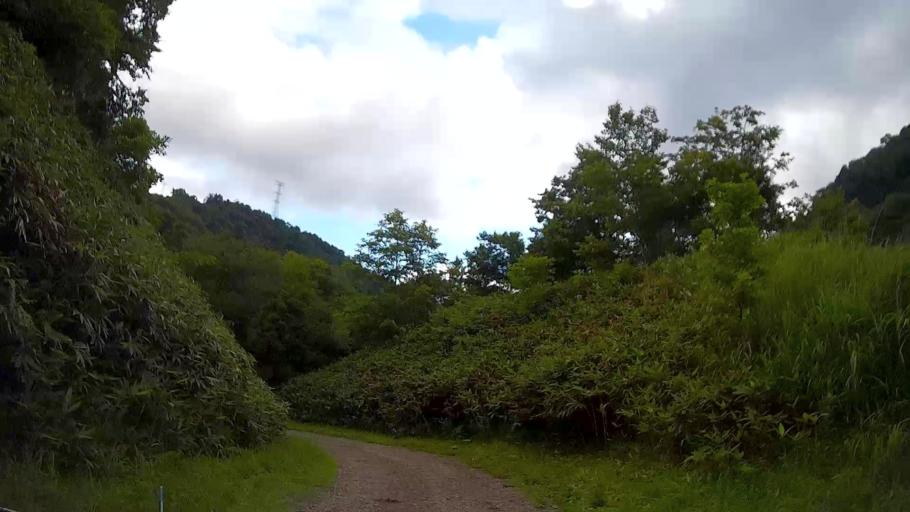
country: JP
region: Hokkaido
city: Nanae
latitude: 42.0384
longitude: 140.4833
